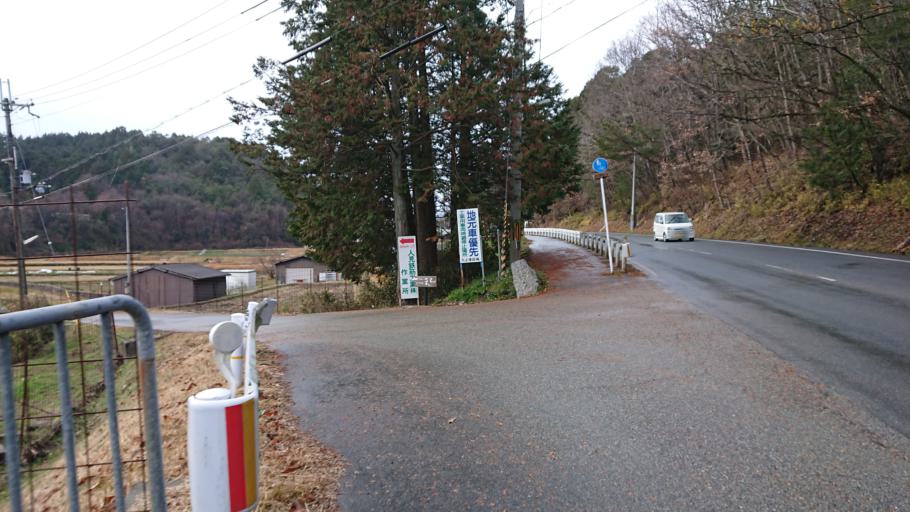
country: JP
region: Kyoto
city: Kameoka
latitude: 35.0528
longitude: 135.5210
